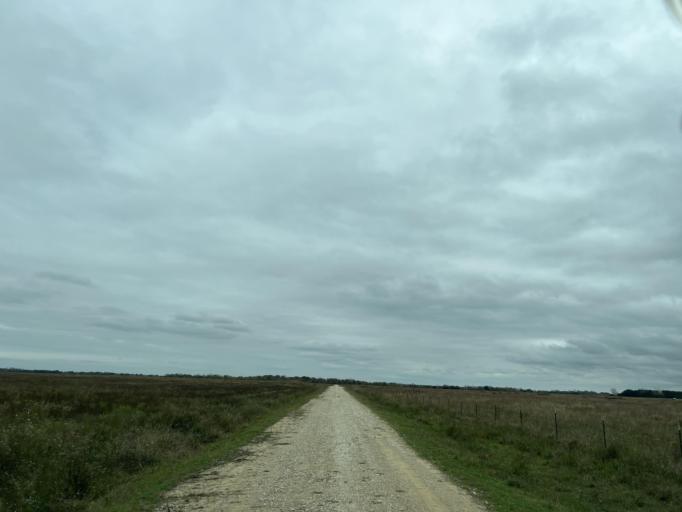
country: US
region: Texas
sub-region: Colorado County
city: Eagle Lake
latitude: 29.6665
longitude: -96.2790
